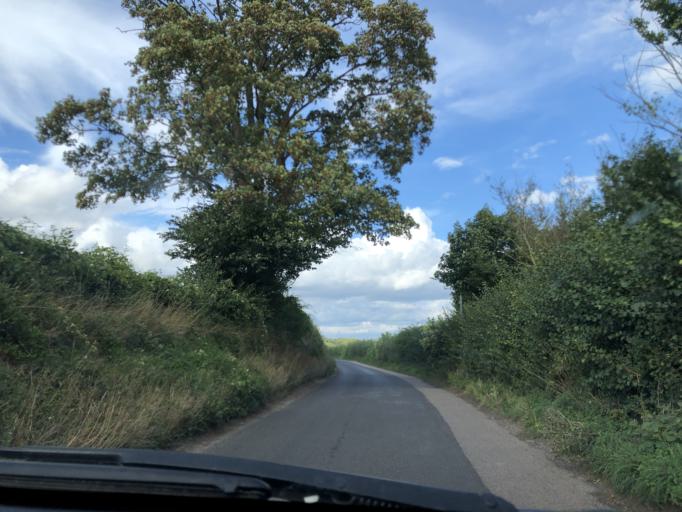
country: GB
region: England
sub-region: Kent
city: Eynsford
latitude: 51.3752
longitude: 0.2136
